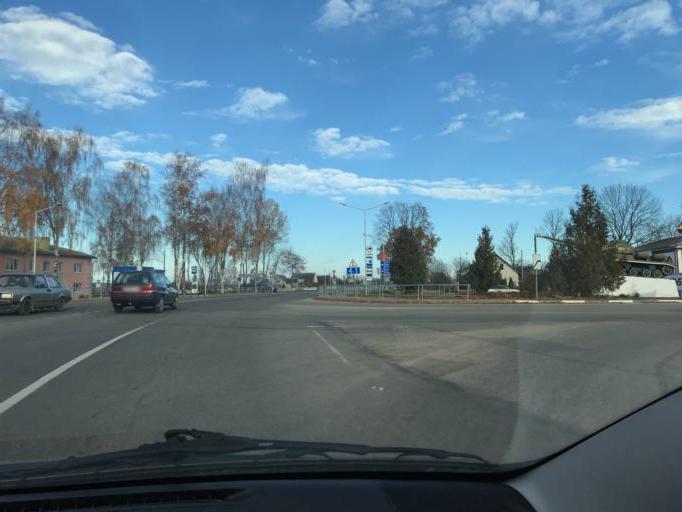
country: BY
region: Vitebsk
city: Haradok
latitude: 55.4707
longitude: 29.9707
